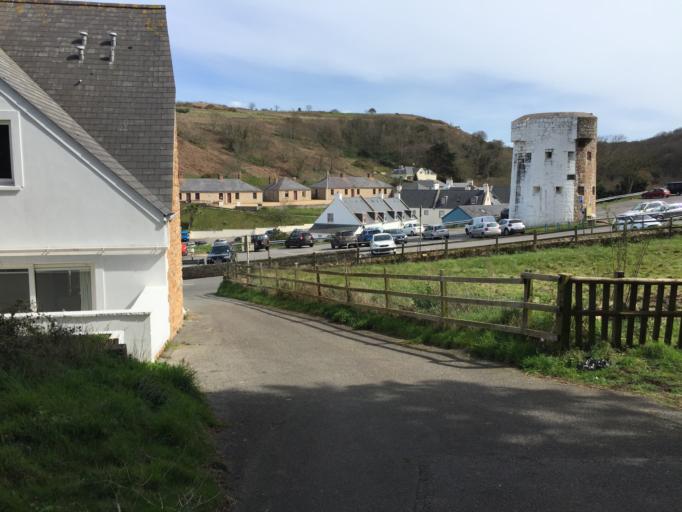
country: JE
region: St Helier
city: Saint Helier
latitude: 49.2463
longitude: -2.2017
